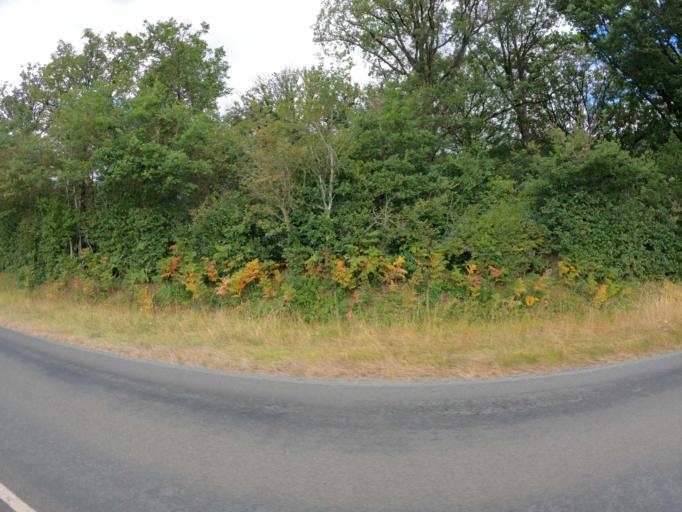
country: FR
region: Pays de la Loire
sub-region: Departement de la Sarthe
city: Sable-sur-Sarthe
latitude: 47.8198
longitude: -0.3993
